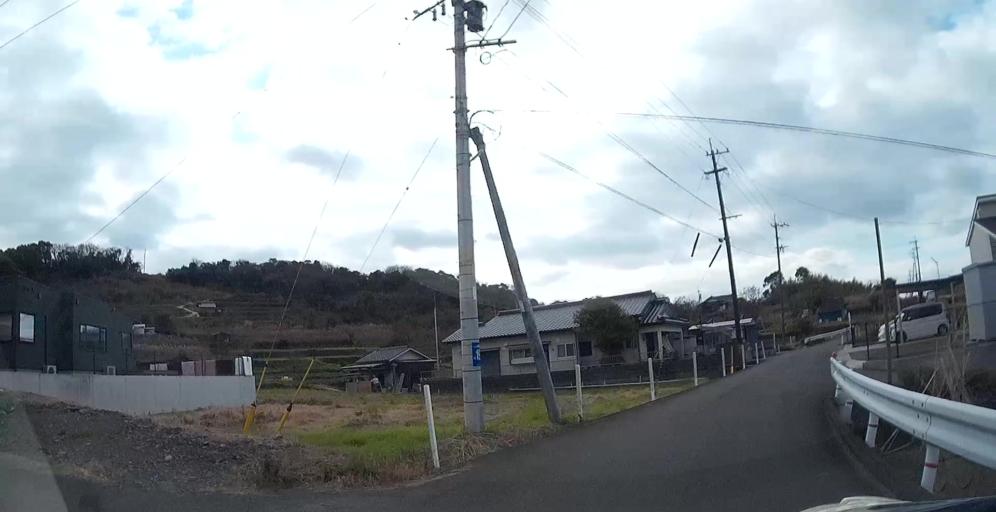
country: JP
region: Kumamoto
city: Minamata
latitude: 32.2077
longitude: 130.3876
